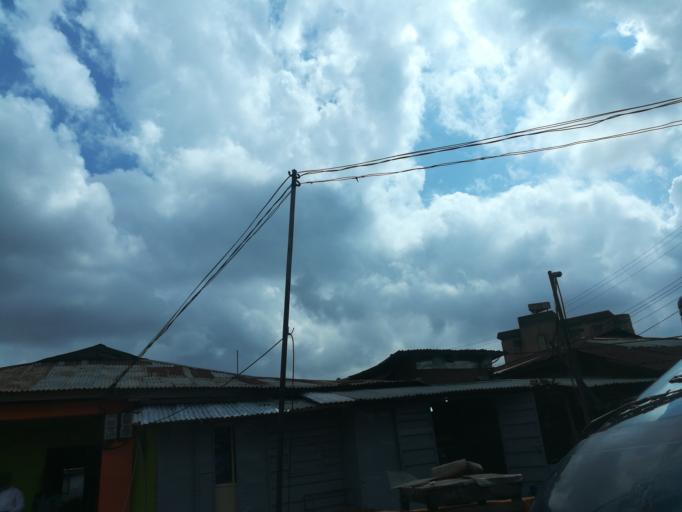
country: NG
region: Lagos
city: Somolu
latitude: 6.5421
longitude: 3.3602
